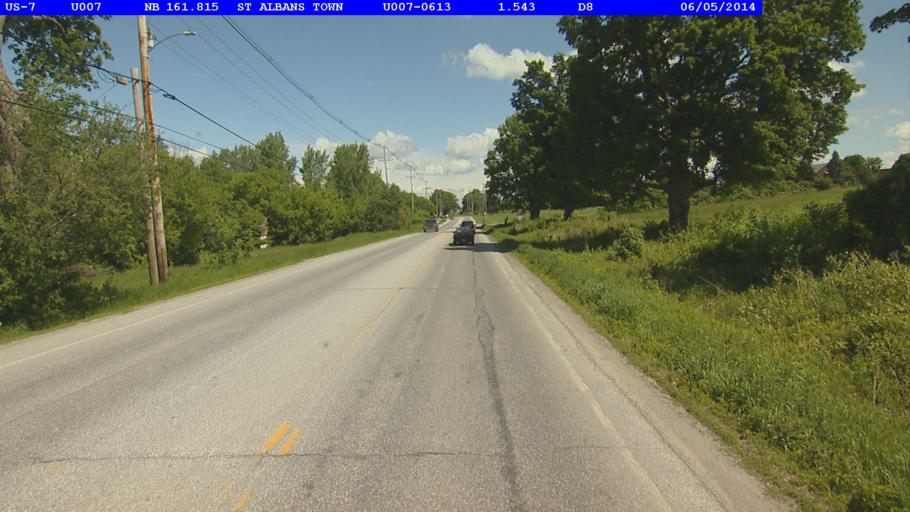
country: US
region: Vermont
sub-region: Franklin County
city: Saint Albans
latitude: 44.8310
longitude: -73.0796
